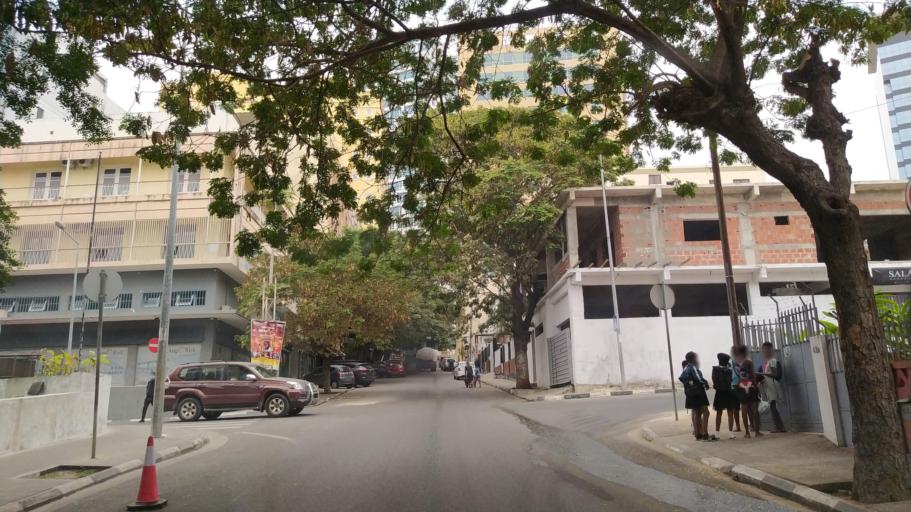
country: AO
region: Luanda
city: Luanda
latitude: -8.8195
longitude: 13.2345
